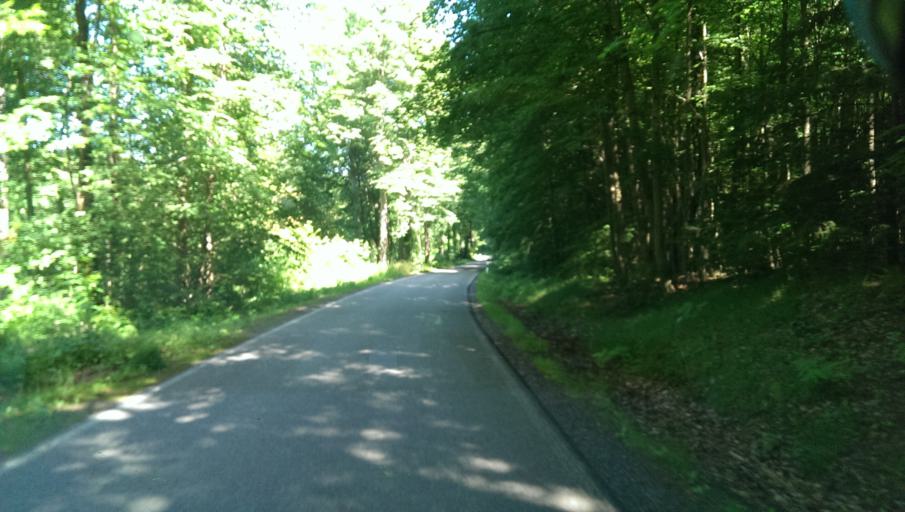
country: DE
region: Rheinland-Pfalz
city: Rumbach
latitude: 49.0856
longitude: 7.7932
